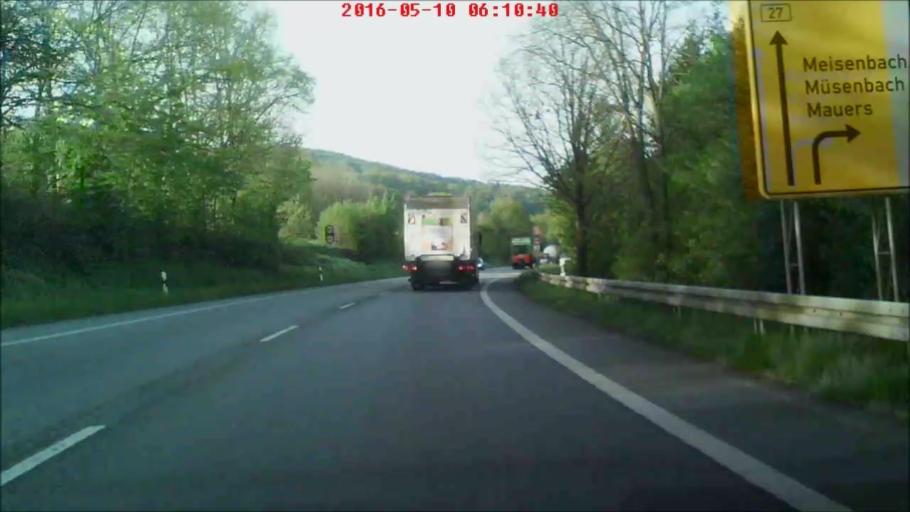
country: DE
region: Hesse
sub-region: Regierungsbezirk Kassel
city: Bad Hersfeld
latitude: 50.7906
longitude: 9.7168
